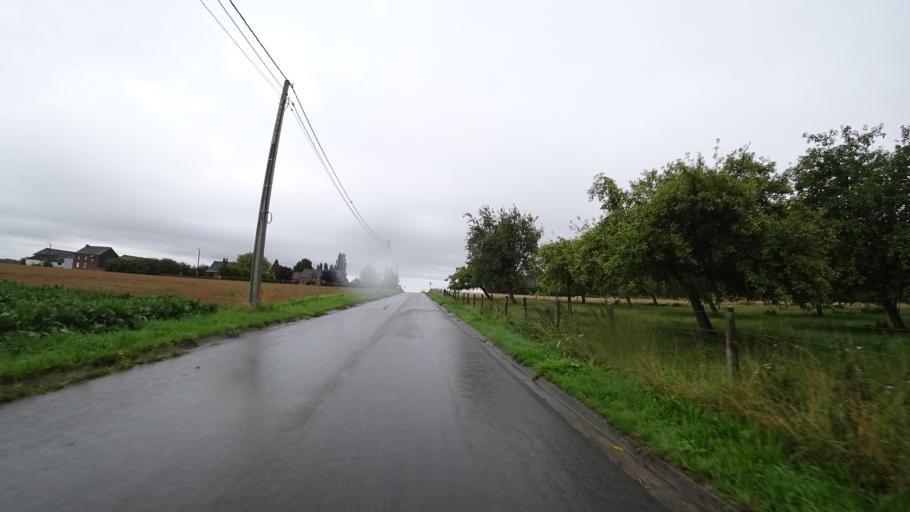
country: BE
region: Wallonia
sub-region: Province de Namur
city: Namur
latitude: 50.5288
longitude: 4.7951
